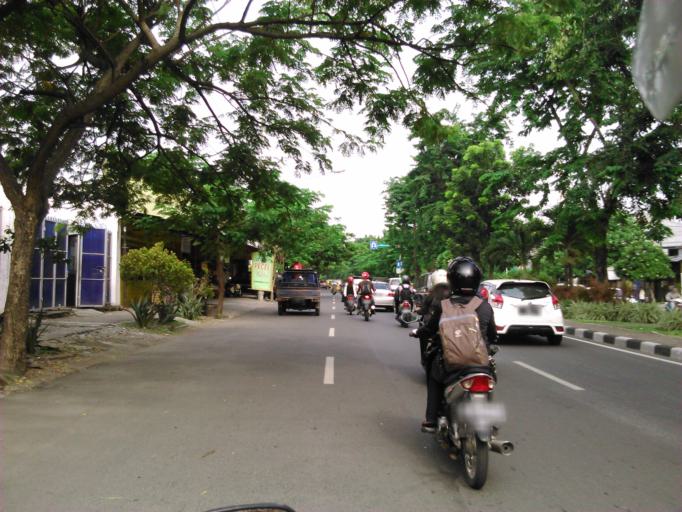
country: ID
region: East Java
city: Brongkalan
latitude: -7.2664
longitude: 112.7670
